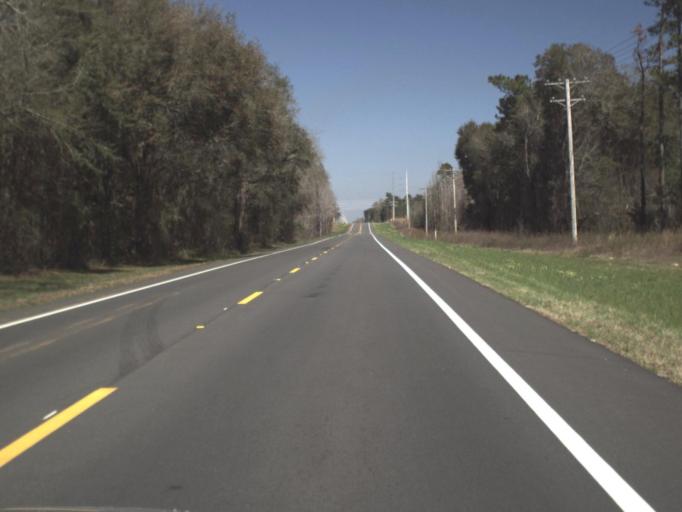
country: US
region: Florida
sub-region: Jackson County
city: Sneads
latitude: 30.7352
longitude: -85.0198
